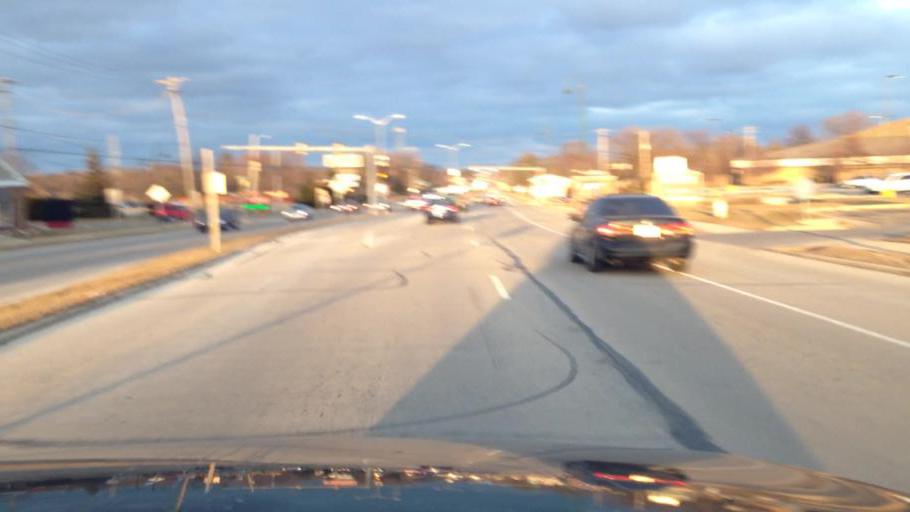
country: US
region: Wisconsin
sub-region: Milwaukee County
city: Greenfield
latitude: 42.9657
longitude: -88.0056
